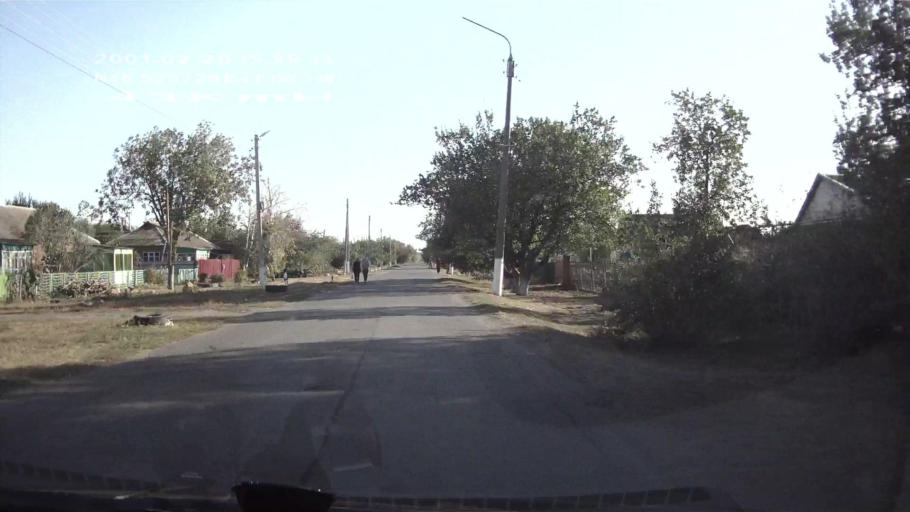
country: RU
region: Rostov
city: Gigant
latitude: 46.5256
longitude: 41.1901
